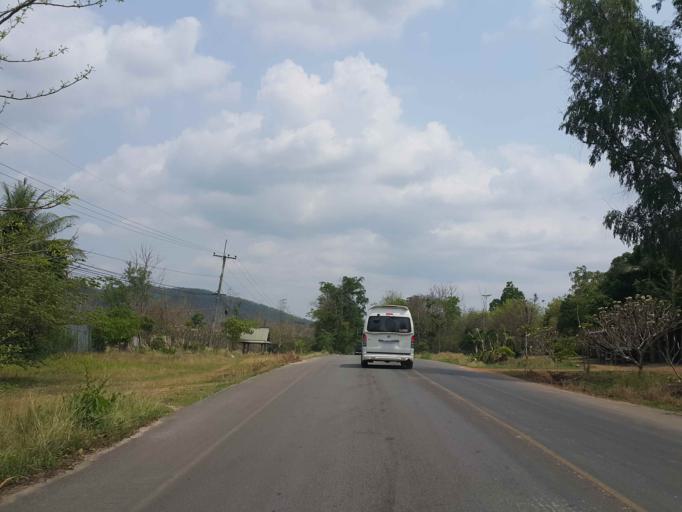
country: TH
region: Lampang
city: Thoen
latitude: 17.5383
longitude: 99.3406
